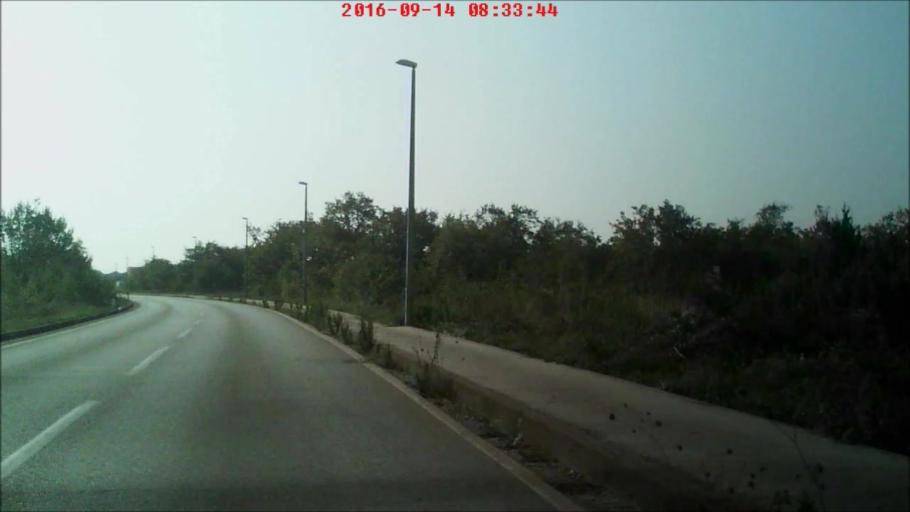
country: HR
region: Zadarska
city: Policnik
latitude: 44.1543
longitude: 15.3140
